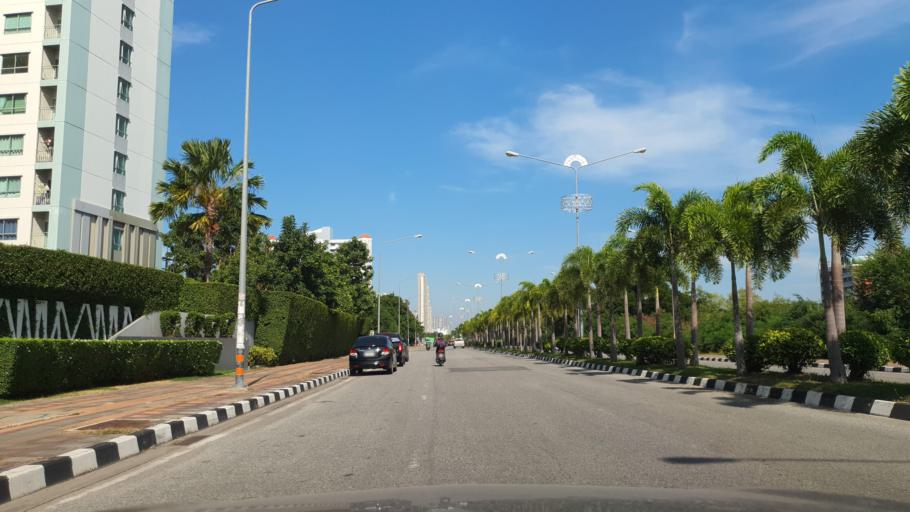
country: TH
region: Chon Buri
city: Phatthaya
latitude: 12.8713
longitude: 100.8940
